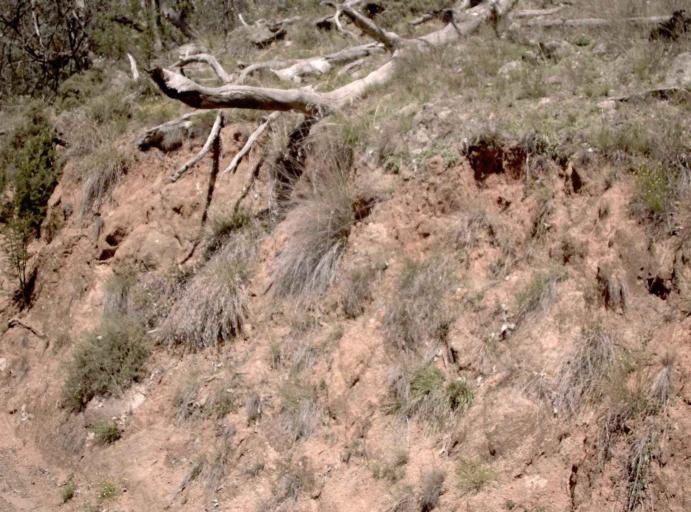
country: AU
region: New South Wales
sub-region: Snowy River
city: Jindabyne
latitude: -37.0552
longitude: 148.5359
